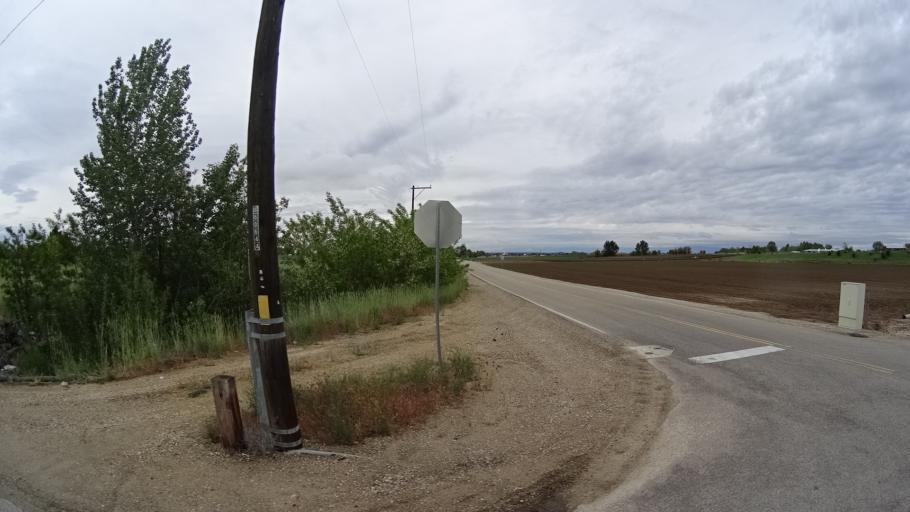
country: US
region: Idaho
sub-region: Ada County
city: Star
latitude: 43.7211
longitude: -116.4682
